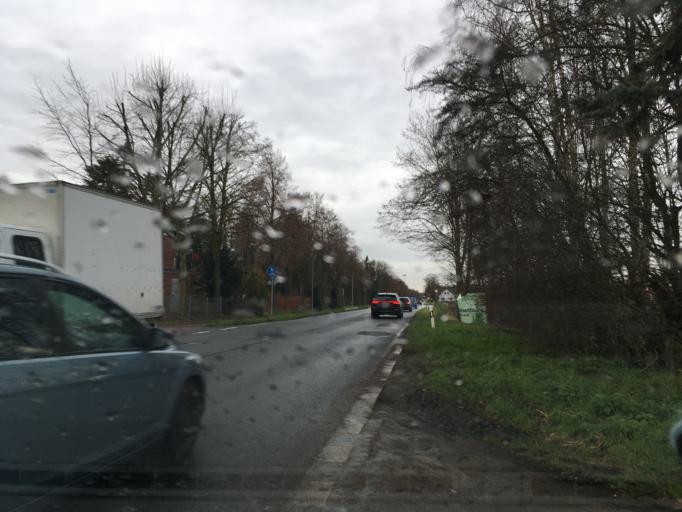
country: DE
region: North Rhine-Westphalia
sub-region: Regierungsbezirk Munster
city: Gescher
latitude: 51.9458
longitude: 7.0200
